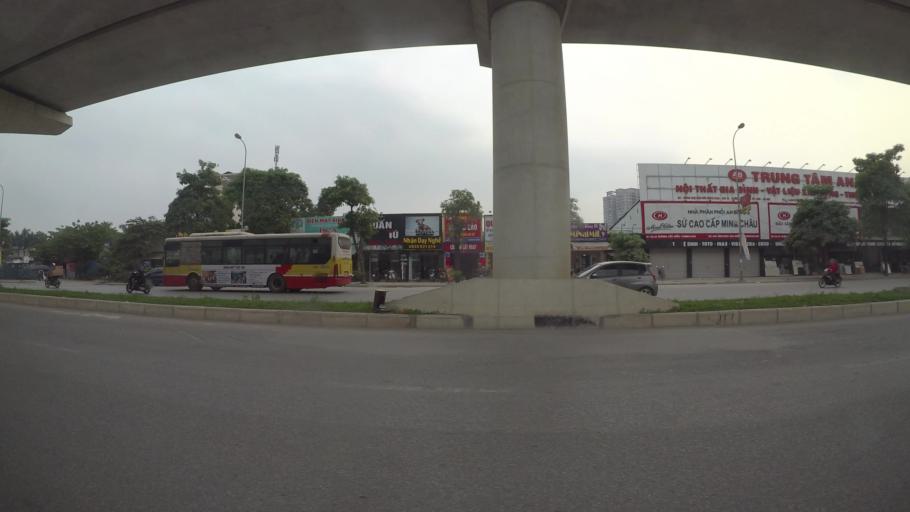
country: VN
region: Ha Noi
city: Cau Dien
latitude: 21.0507
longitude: 105.7383
